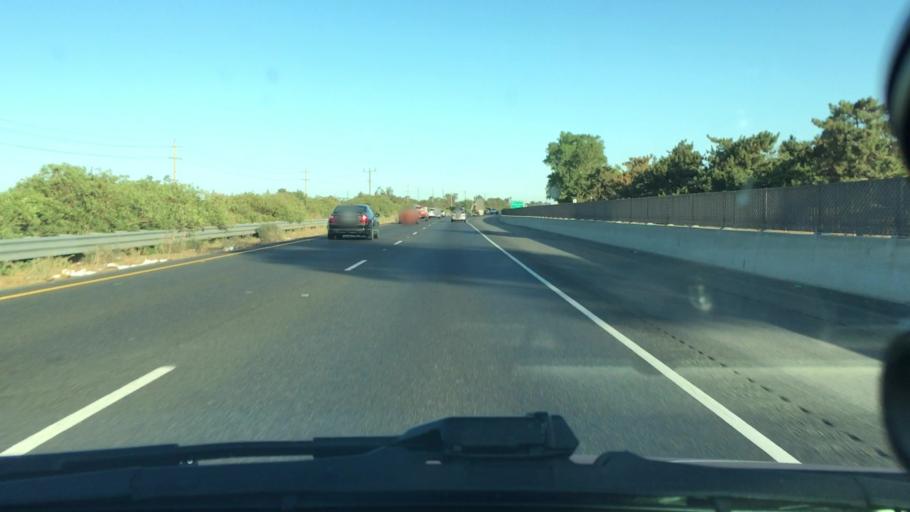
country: US
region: California
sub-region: Sacramento County
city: Elk Grove
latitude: 38.3901
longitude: -121.3753
